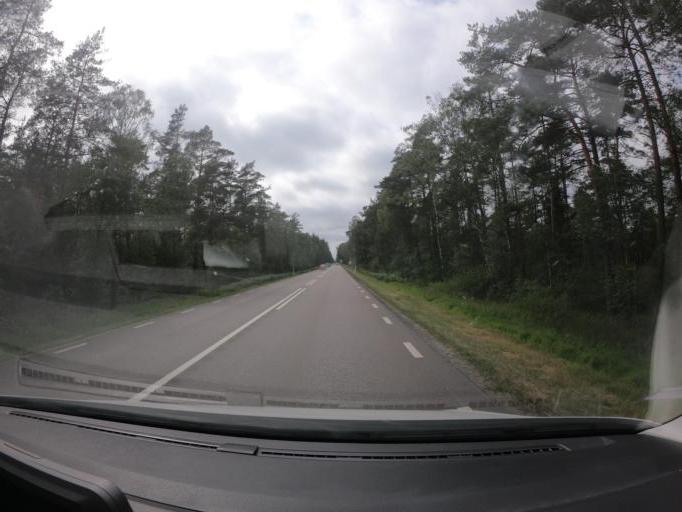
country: SE
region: Skane
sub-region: Perstorps Kommun
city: Perstorp
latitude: 56.2417
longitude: 13.4903
